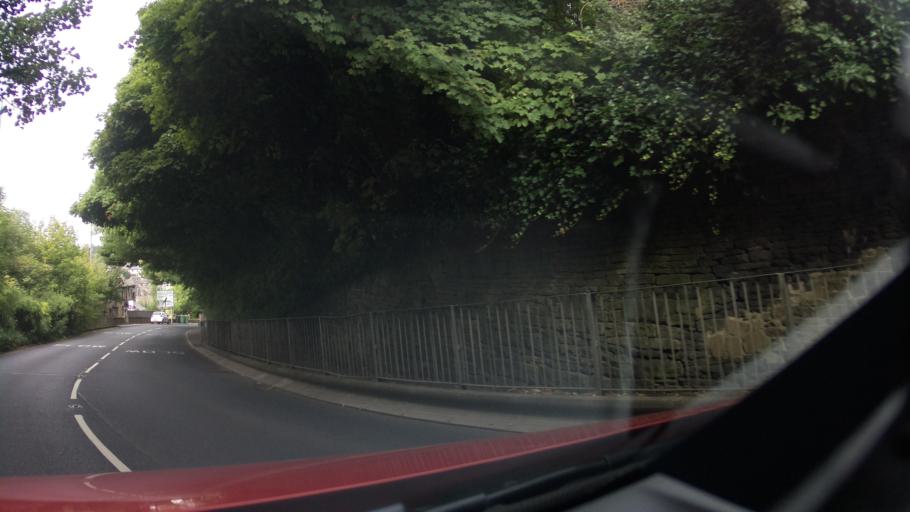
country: GB
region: England
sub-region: Kirklees
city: Holmfirth
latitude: 53.5743
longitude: -1.7527
